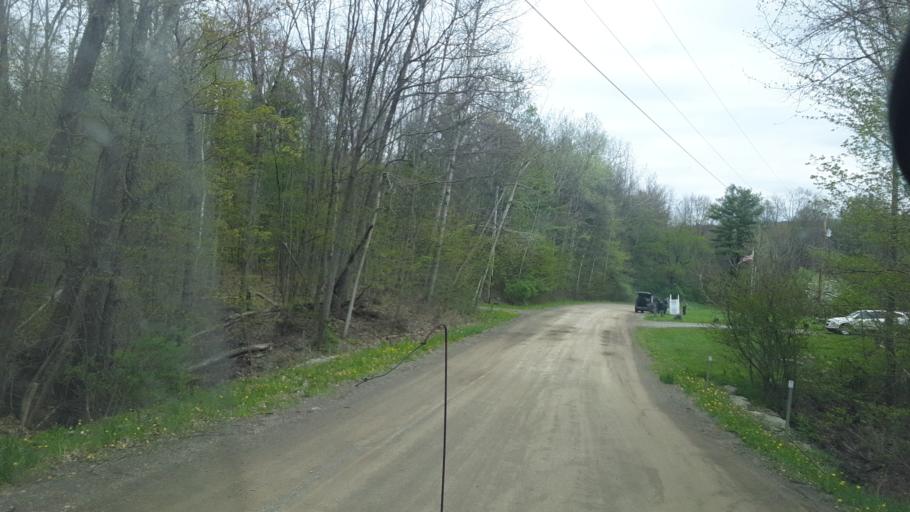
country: US
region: New York
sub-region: Steuben County
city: Addison
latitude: 42.0968
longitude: -77.3173
